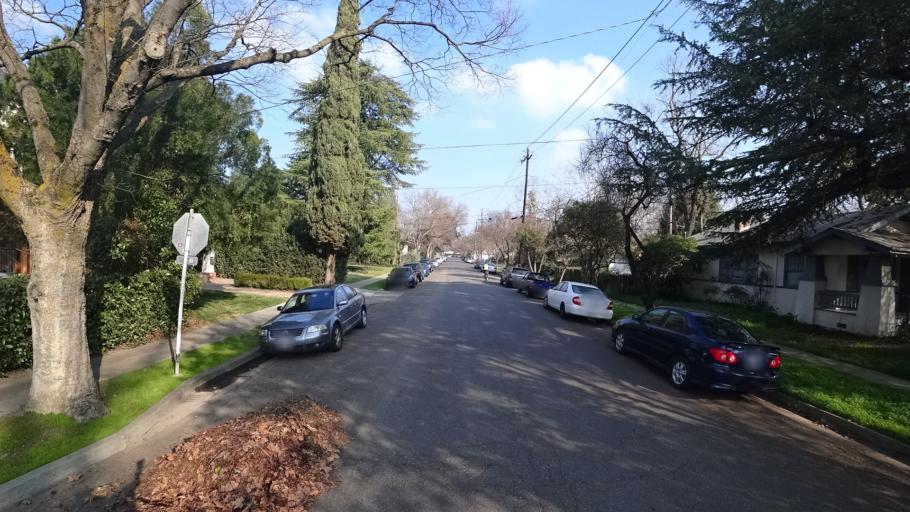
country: US
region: California
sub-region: Yolo County
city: Davis
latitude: 38.5498
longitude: -121.7440
